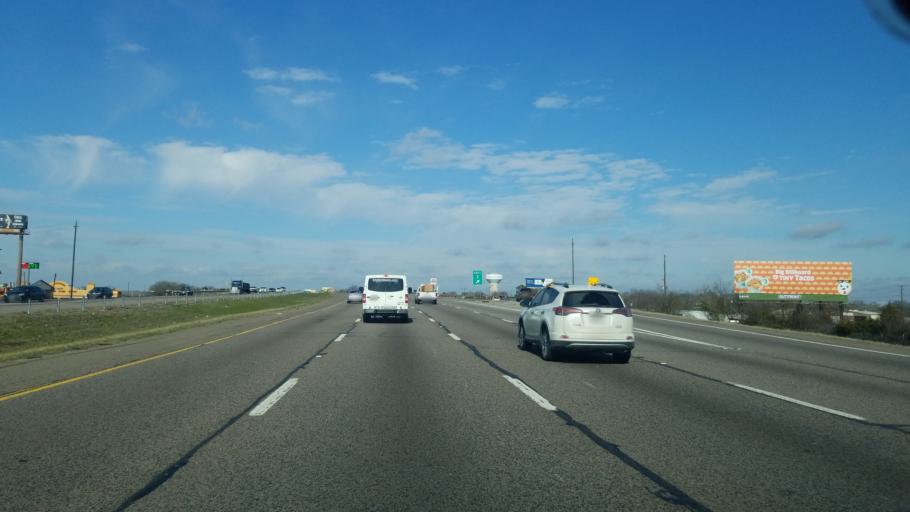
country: US
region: Texas
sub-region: Dallas County
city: Balch Springs
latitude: 32.7316
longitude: -96.6126
